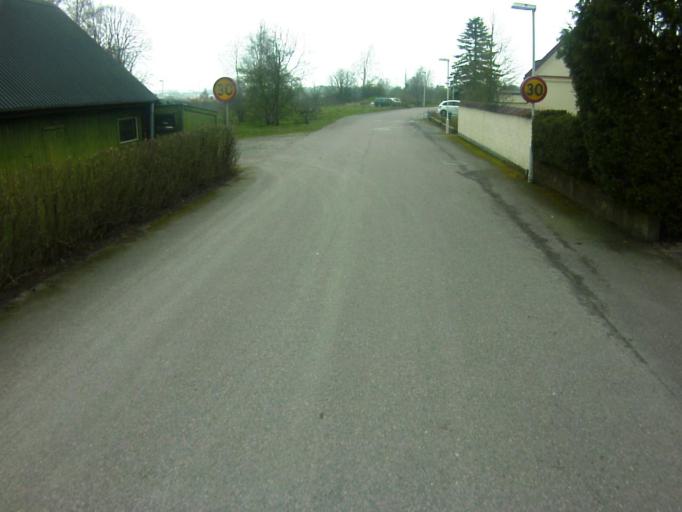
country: SE
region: Skane
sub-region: Kavlinge Kommun
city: Kaevlinge
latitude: 55.7762
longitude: 13.0998
